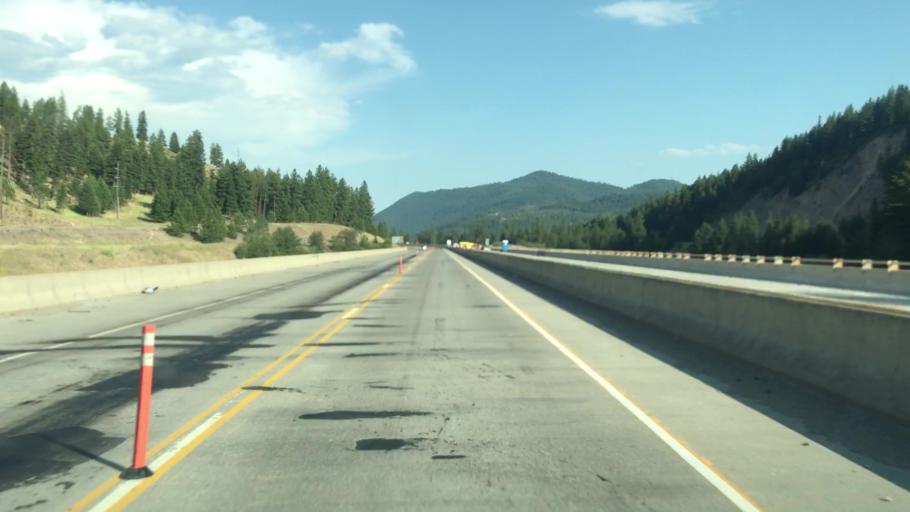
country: US
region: Montana
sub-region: Mineral County
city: Superior
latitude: 47.2213
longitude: -114.9616
